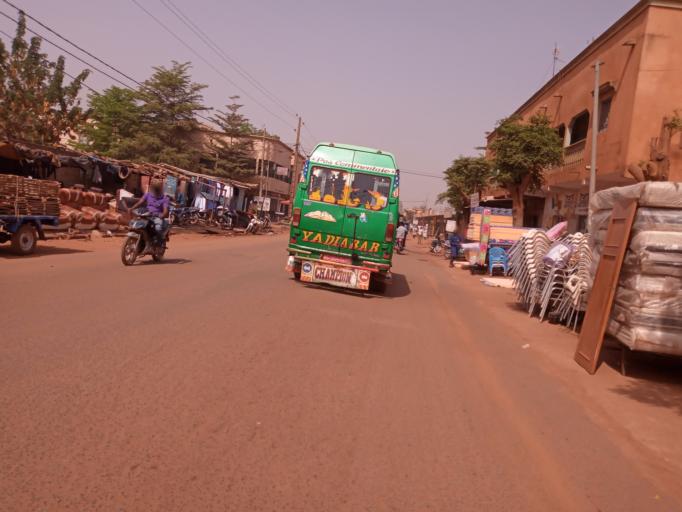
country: ML
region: Bamako
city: Bamako
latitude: 12.5884
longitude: -7.9713
